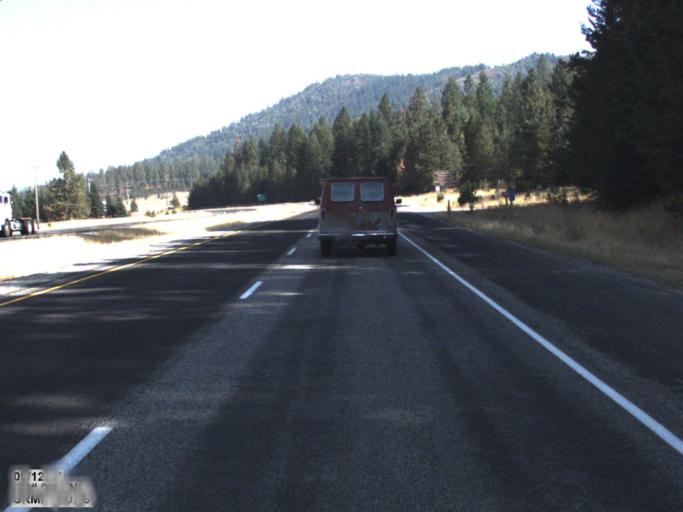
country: US
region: Washington
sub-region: Spokane County
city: Deer Park
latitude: 48.0976
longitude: -117.2936
